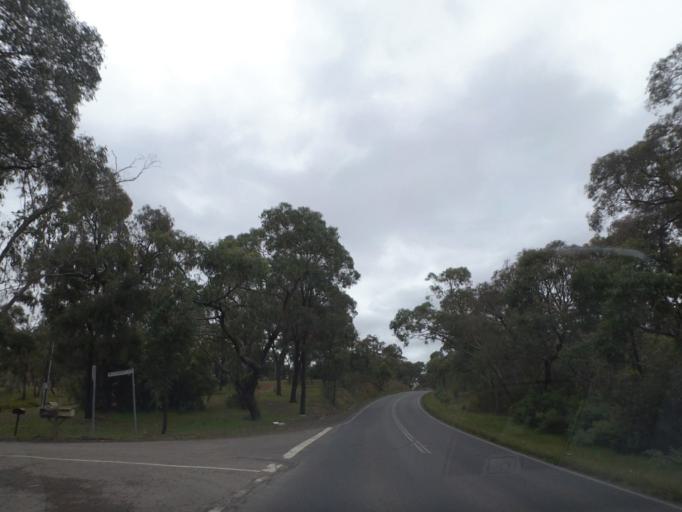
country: AU
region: Victoria
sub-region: Nillumbik
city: Diamond Creek
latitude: -37.6510
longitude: 145.1463
